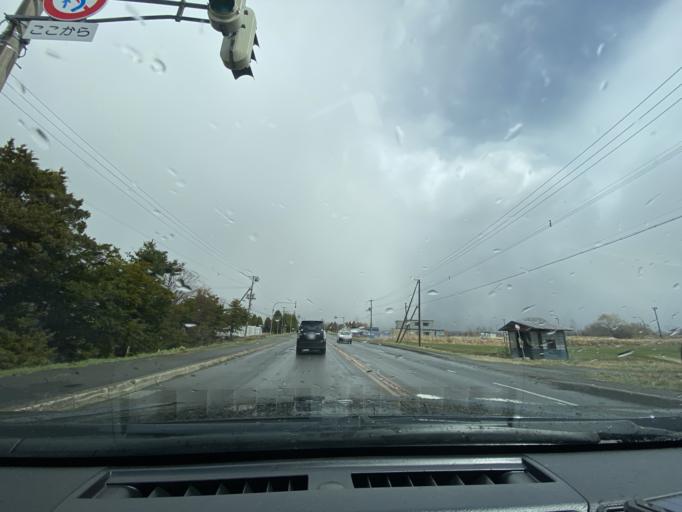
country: JP
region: Hokkaido
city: Takikawa
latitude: 43.6034
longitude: 141.9304
